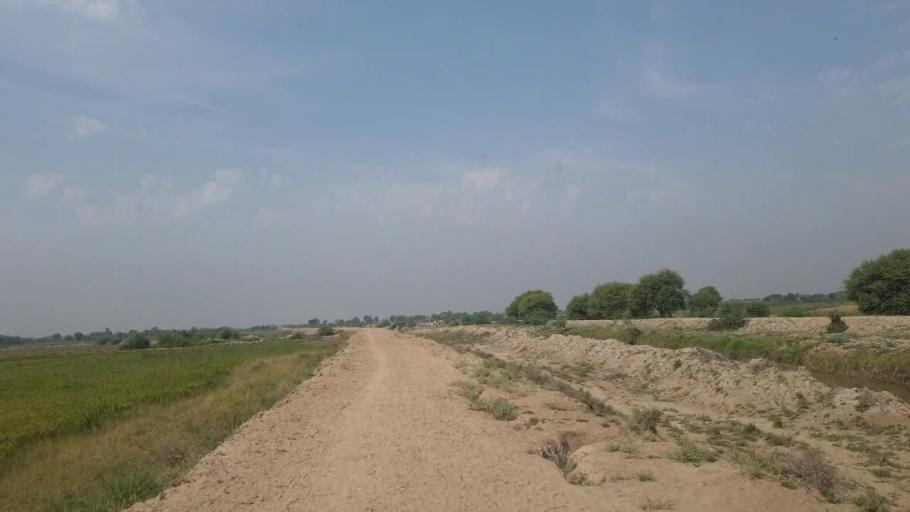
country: PK
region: Sindh
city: Rajo Khanani
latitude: 24.9570
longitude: 69.0278
